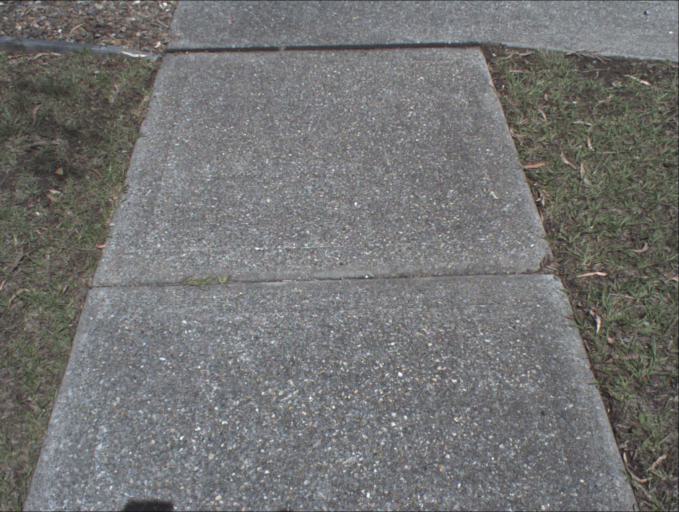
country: AU
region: Queensland
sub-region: Logan
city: Waterford West
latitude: -27.6815
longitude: 153.1477
